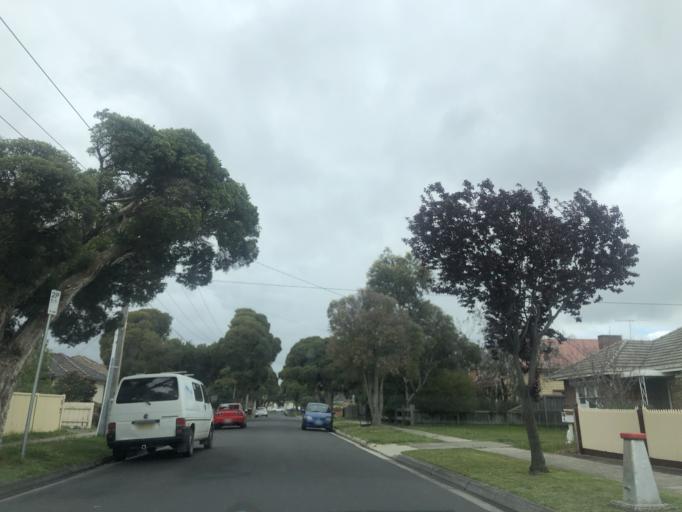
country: AU
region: Victoria
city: Clayton
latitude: -37.9239
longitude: 145.1152
